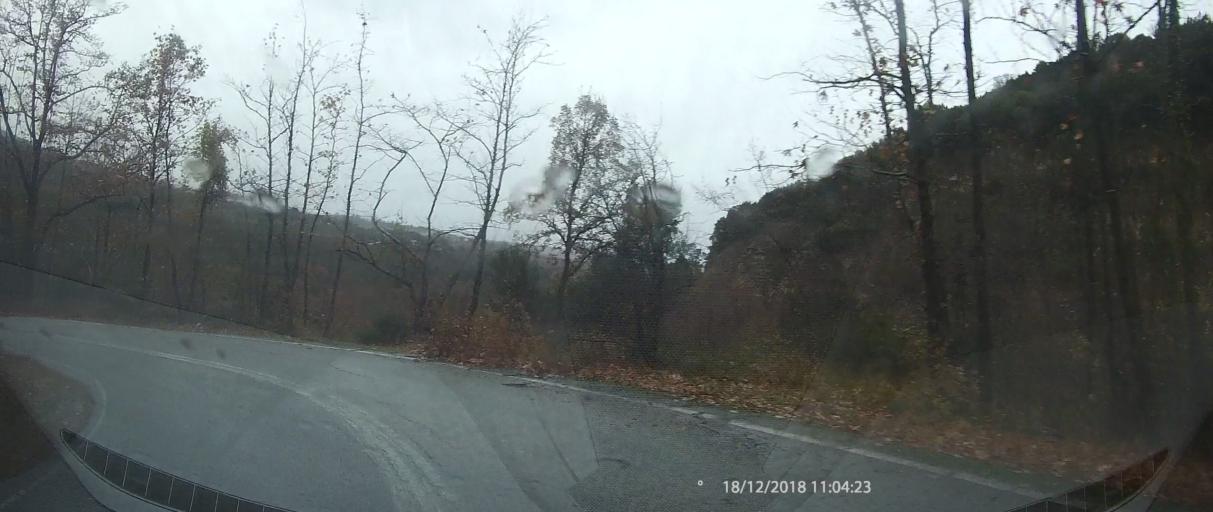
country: GR
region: Central Macedonia
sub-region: Nomos Pierias
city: Kato Milia
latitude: 40.2100
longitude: 22.3183
